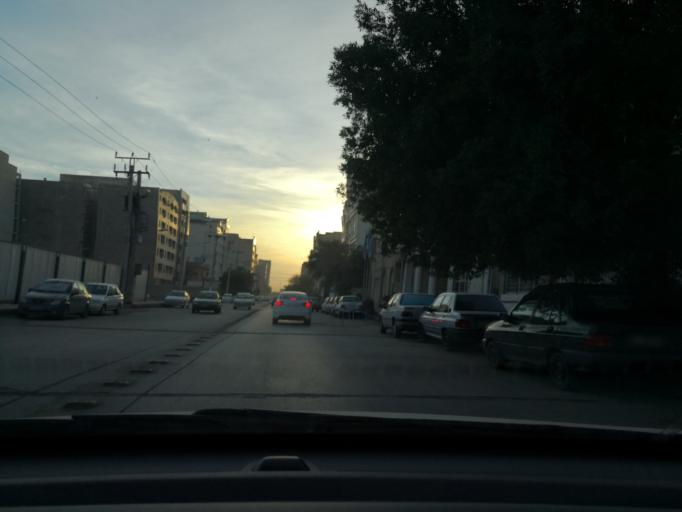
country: IR
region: Khuzestan
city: Ahvaz
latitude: 31.3499
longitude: 48.6884
